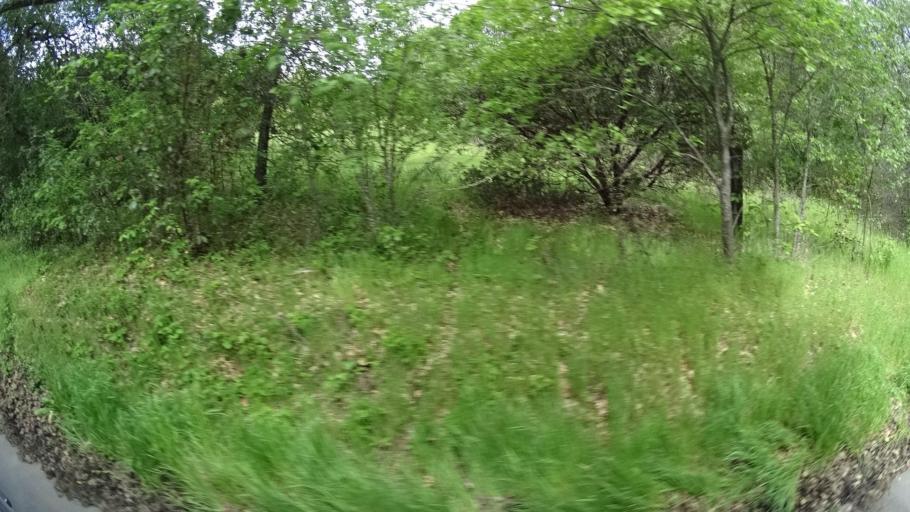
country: US
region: California
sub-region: Humboldt County
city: Redway
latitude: 40.1696
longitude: -123.6099
